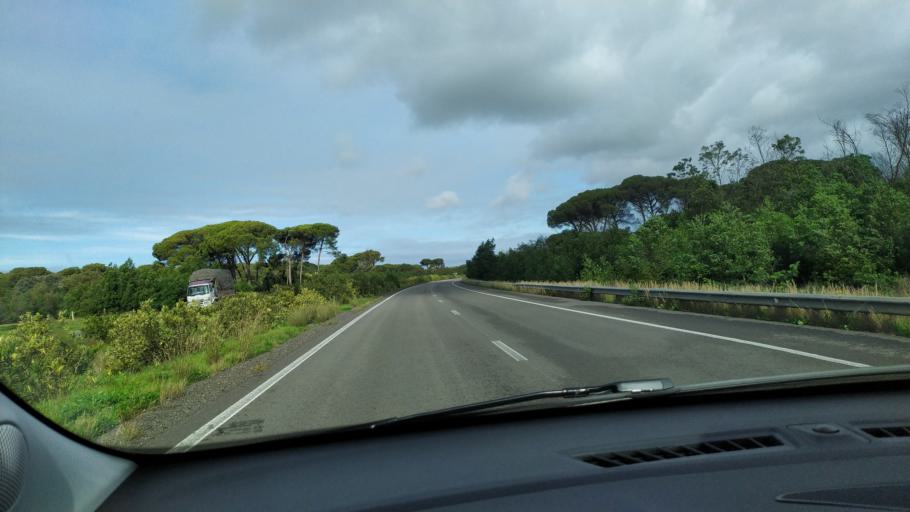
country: MA
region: Tanger-Tetouan
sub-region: Larache
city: Larache
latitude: 35.1305
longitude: -6.1465
